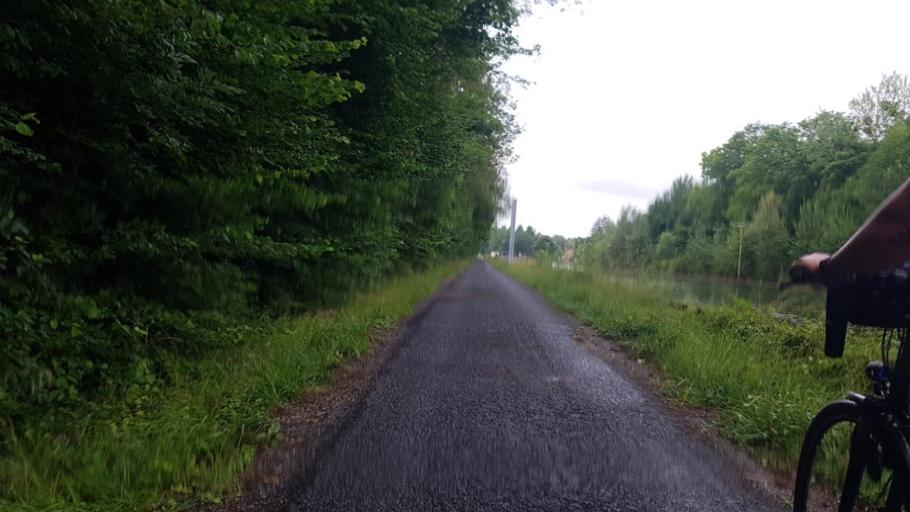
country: FR
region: Champagne-Ardenne
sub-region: Departement de la Marne
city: Vitry-le-Francois
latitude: 48.7473
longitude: 4.5760
